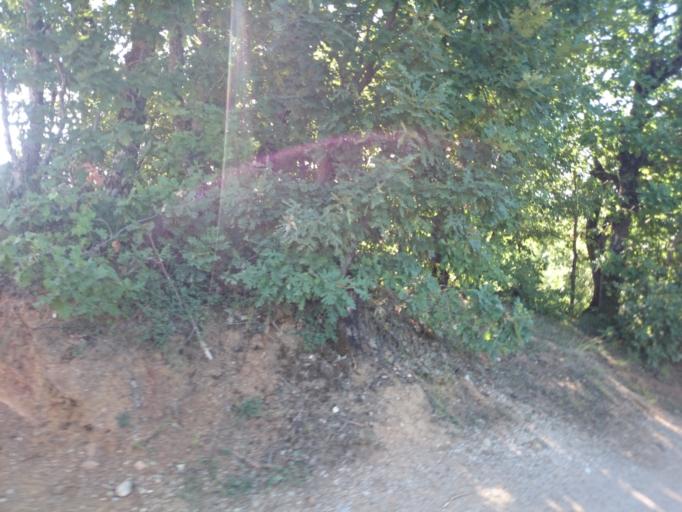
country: AL
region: Diber
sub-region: Rrethi i Bulqizes
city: Zerqan
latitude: 41.5000
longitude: 20.3843
